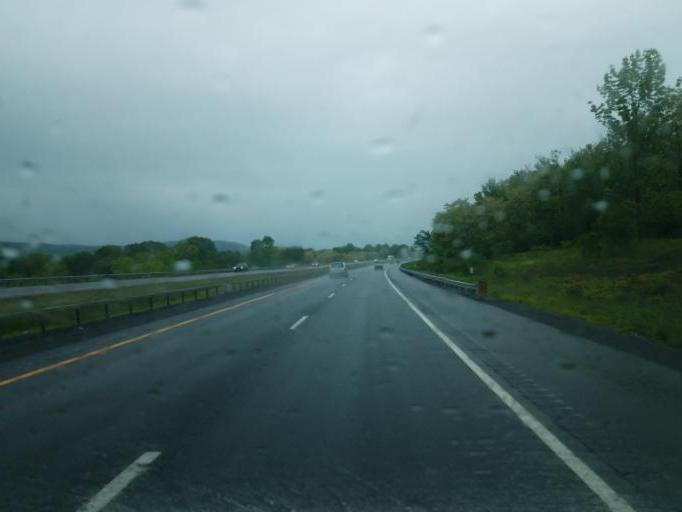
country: US
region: New York
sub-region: Herkimer County
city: Ilion
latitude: 43.0311
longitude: -75.0431
